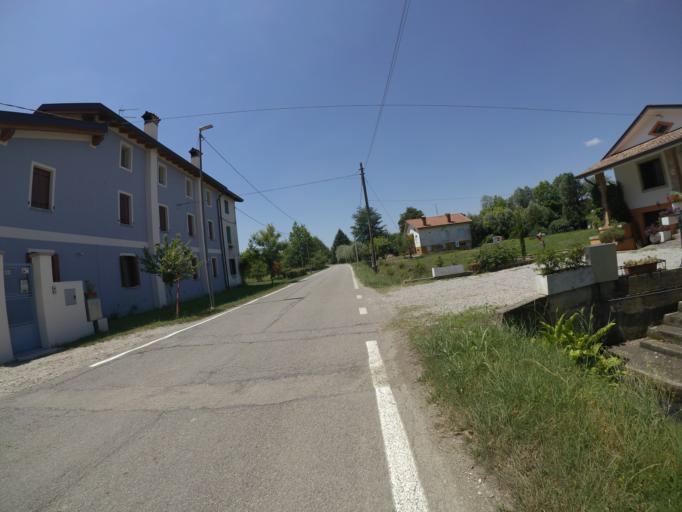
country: IT
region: Friuli Venezia Giulia
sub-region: Provincia di Udine
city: Rivignano
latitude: 45.9018
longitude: 13.0266
